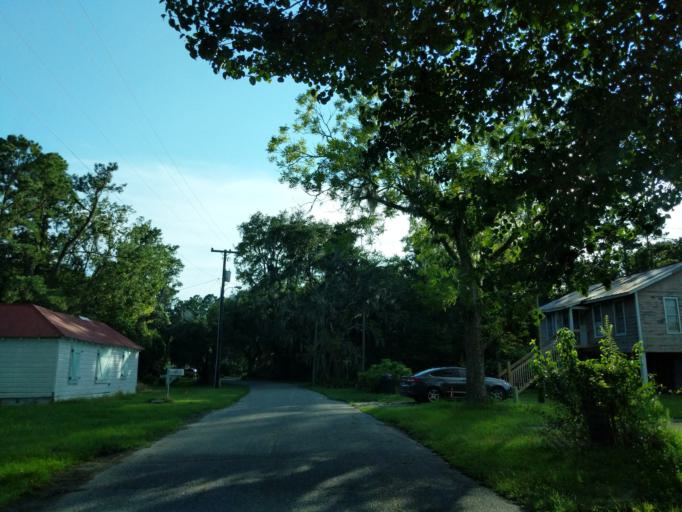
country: US
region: South Carolina
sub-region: Charleston County
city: Awendaw
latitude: 33.0887
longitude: -79.4638
